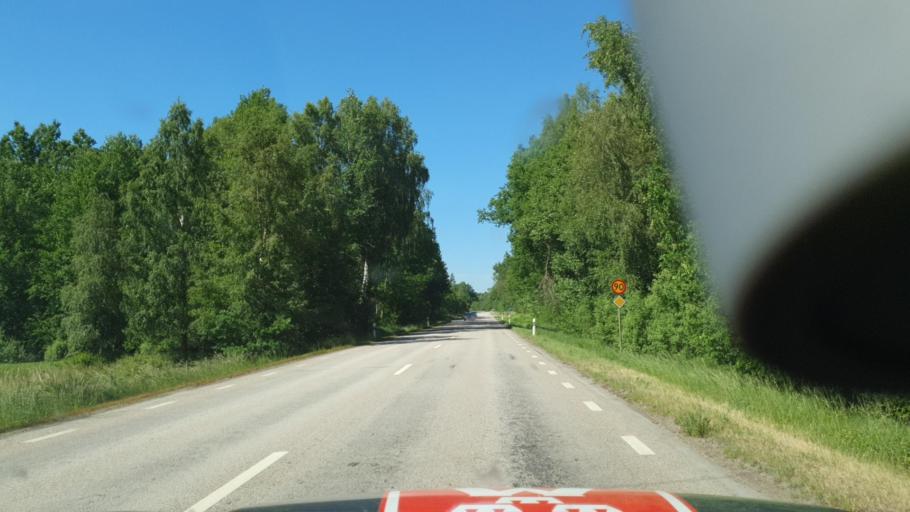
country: SE
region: Kalmar
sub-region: Emmaboda Kommun
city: Emmaboda
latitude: 56.5423
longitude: 15.6126
